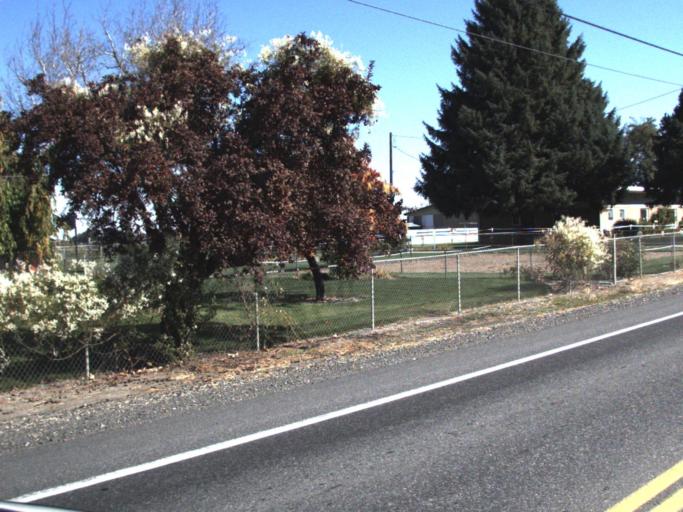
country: US
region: Washington
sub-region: Walla Walla County
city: Burbank
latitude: 46.2117
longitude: -119.0036
